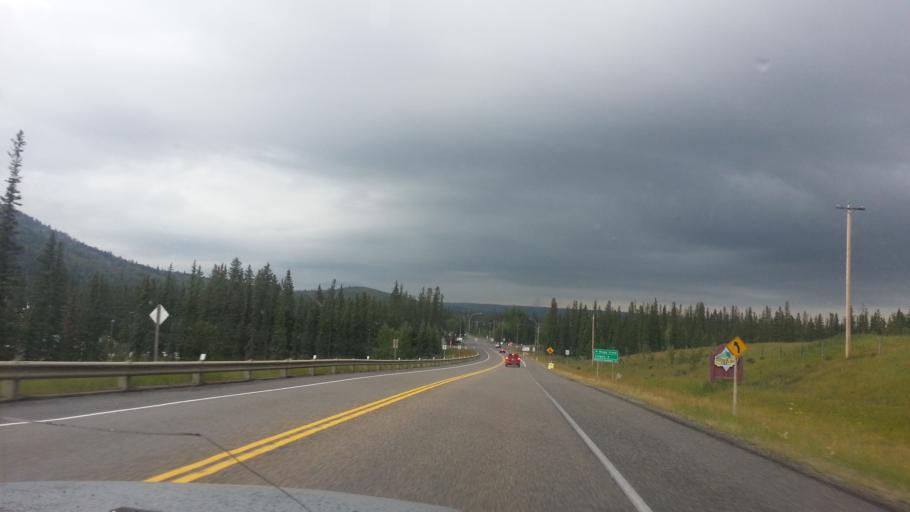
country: CA
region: Alberta
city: Cochrane
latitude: 50.9477
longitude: -114.5607
